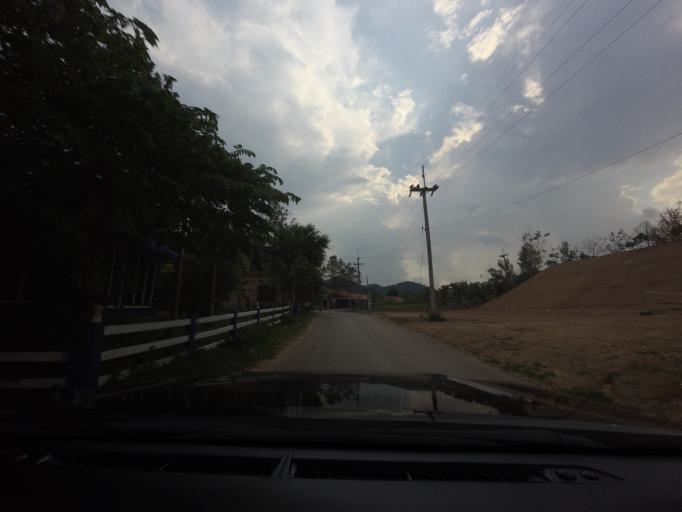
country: TH
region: Nakhon Ratchasima
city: Wang Nam Khiao
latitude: 14.3994
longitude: 101.7922
